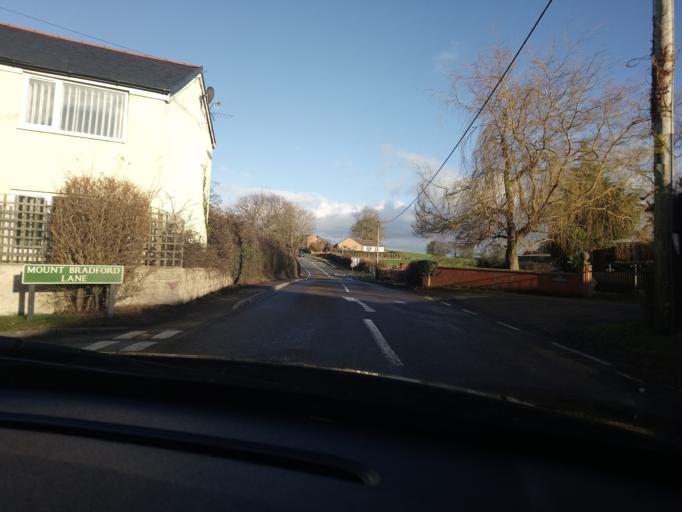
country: GB
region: England
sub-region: Shropshire
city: Gobowen
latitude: 52.9252
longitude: -2.9949
